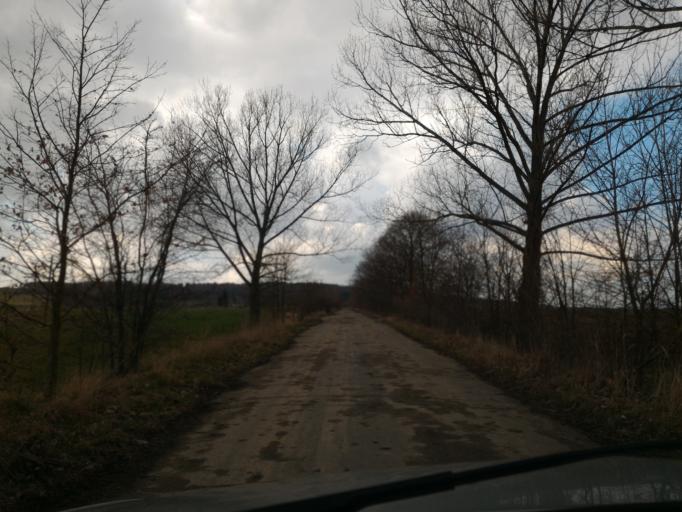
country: PL
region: Lower Silesian Voivodeship
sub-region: Powiat zgorzelecki
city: Bogatynia
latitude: 50.8816
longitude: 14.9266
